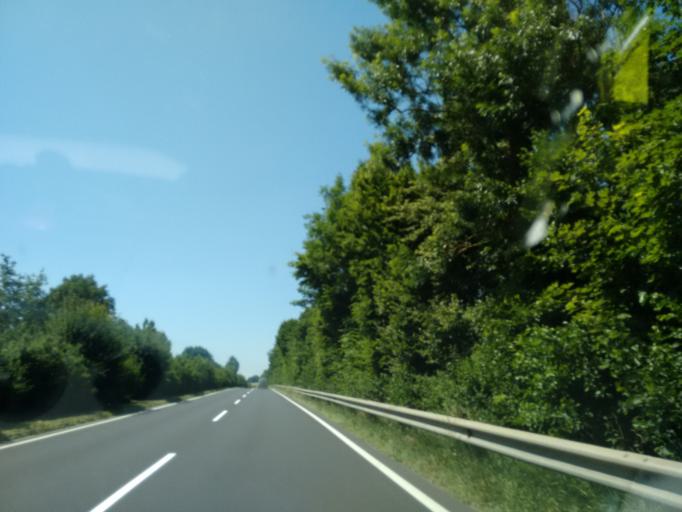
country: AT
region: Upper Austria
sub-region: Wels Stadt
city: Wels
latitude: 48.1885
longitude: 14.0151
